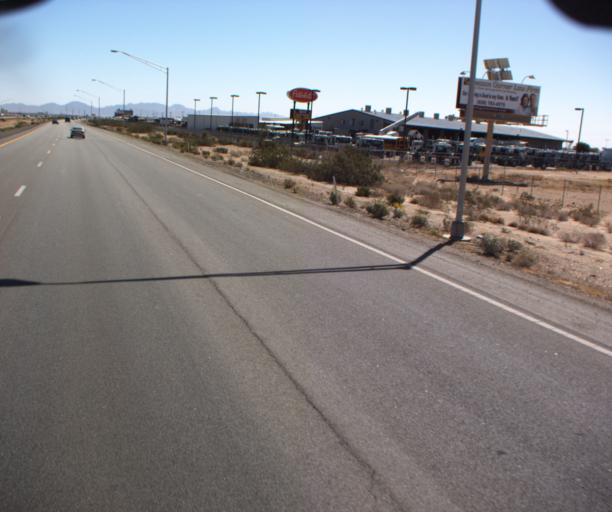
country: US
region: Arizona
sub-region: Yuma County
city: Yuma
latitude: 32.6880
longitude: -114.5766
